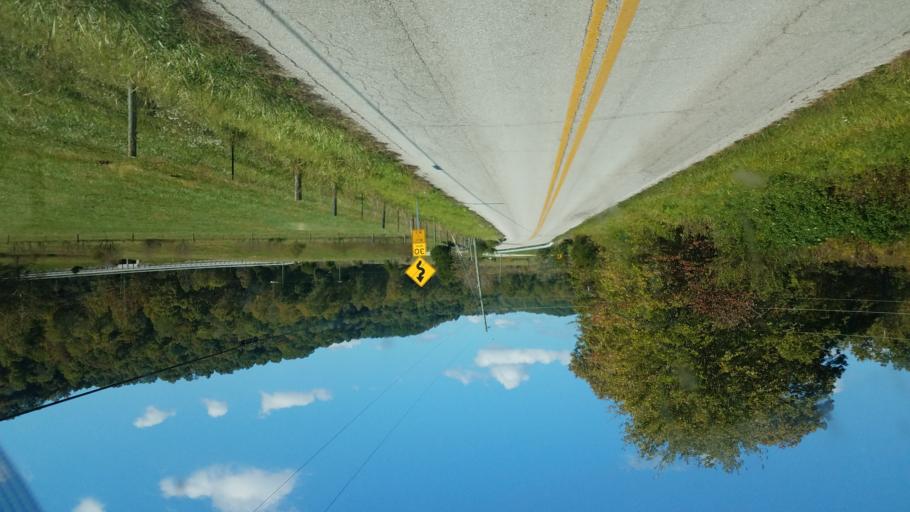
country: US
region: Kentucky
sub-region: Fleming County
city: Flemingsburg
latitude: 38.4691
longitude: -83.5358
